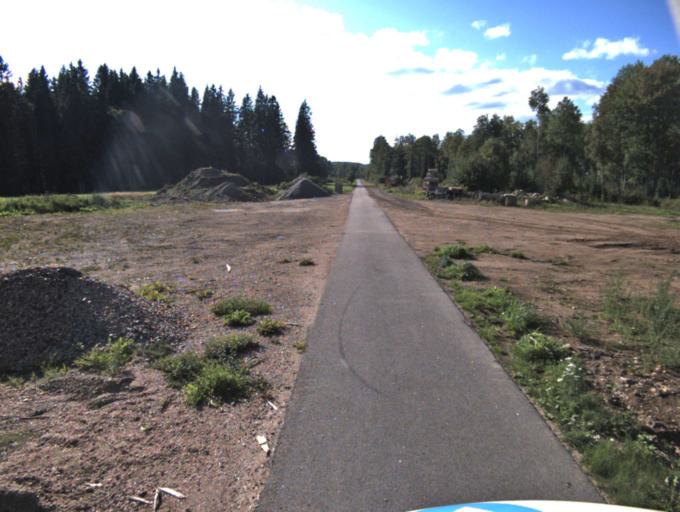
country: SE
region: Vaestra Goetaland
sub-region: Boras Kommun
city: Dalsjofors
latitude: 57.8248
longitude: 13.1718
